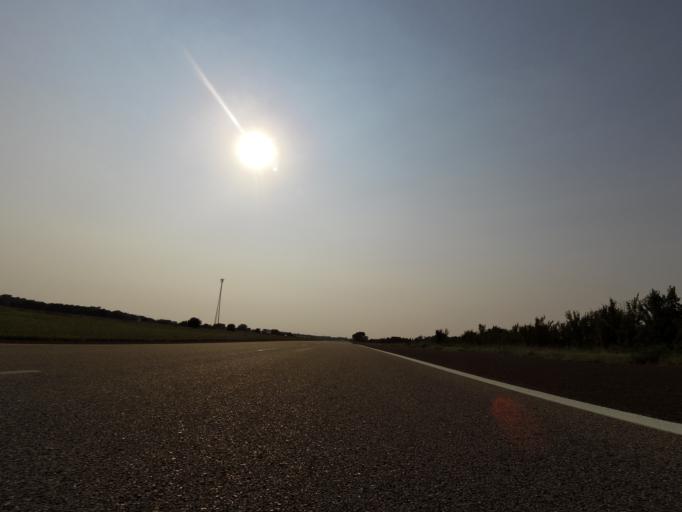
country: US
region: Kansas
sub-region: Reno County
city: Haven
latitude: 37.8940
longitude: -97.7656
